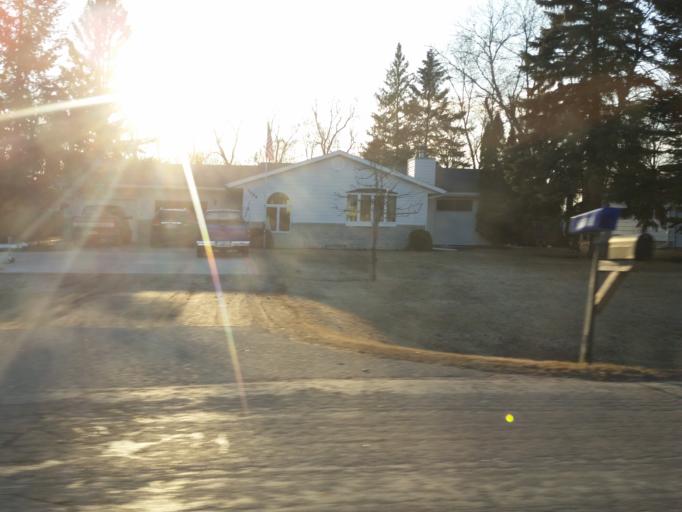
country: US
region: North Dakota
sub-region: Grand Forks County
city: Grand Forks
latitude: 47.8725
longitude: -97.0292
